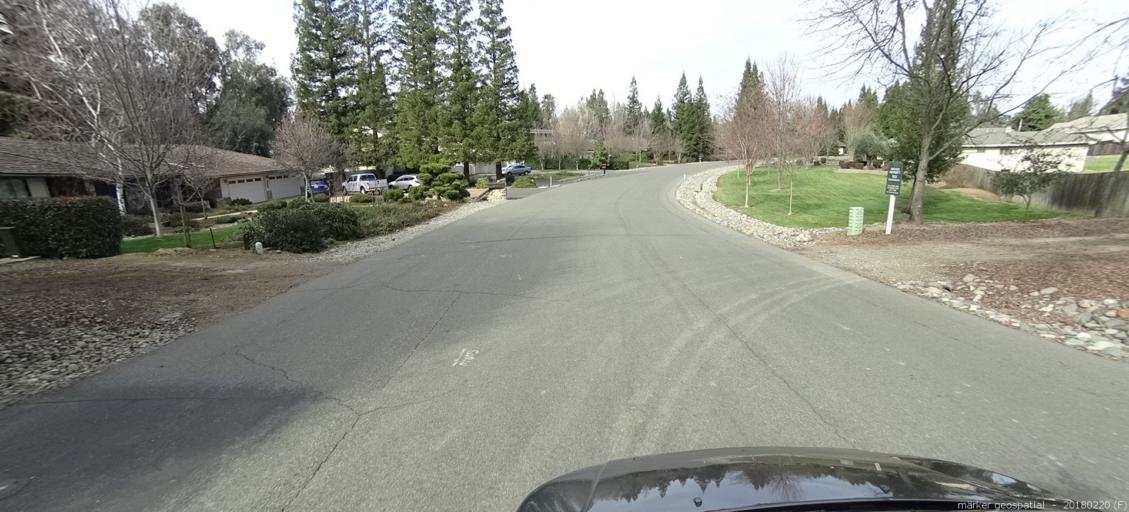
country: US
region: California
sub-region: Sacramento County
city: Orangevale
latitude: 38.7149
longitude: -121.2326
